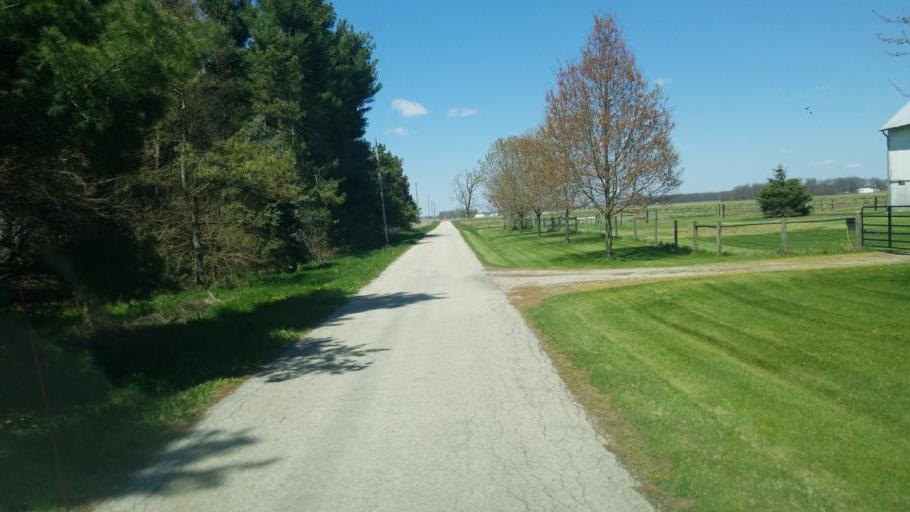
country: US
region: Ohio
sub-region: Marion County
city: Prospect
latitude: 40.4009
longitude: -83.1250
